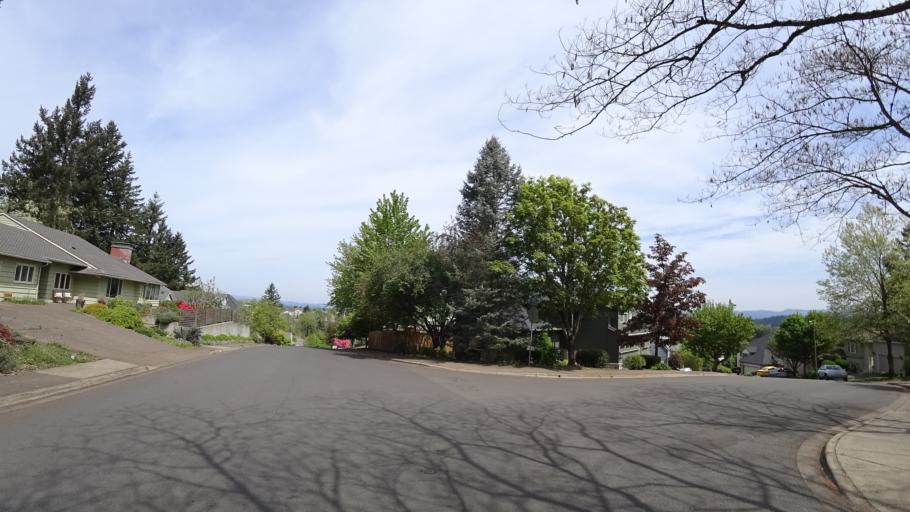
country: US
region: Oregon
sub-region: Washington County
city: Aloha
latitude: 45.4601
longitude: -122.8529
